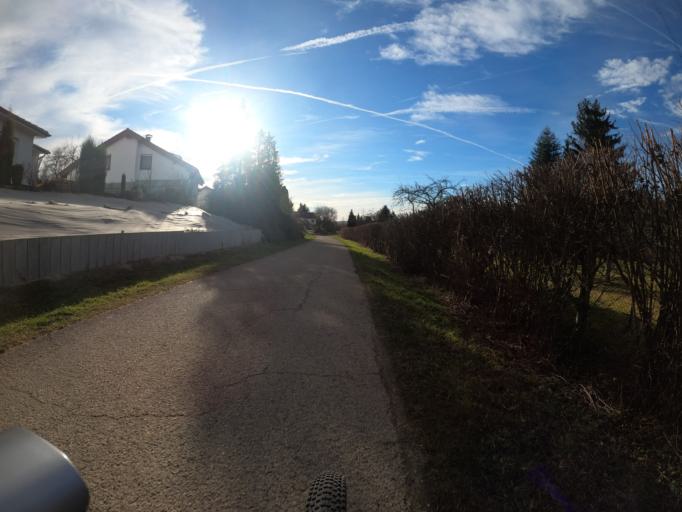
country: DE
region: Baden-Wuerttemberg
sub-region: Regierungsbezirk Stuttgart
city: Kirchheim unter Teck
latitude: 48.6554
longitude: 9.4723
